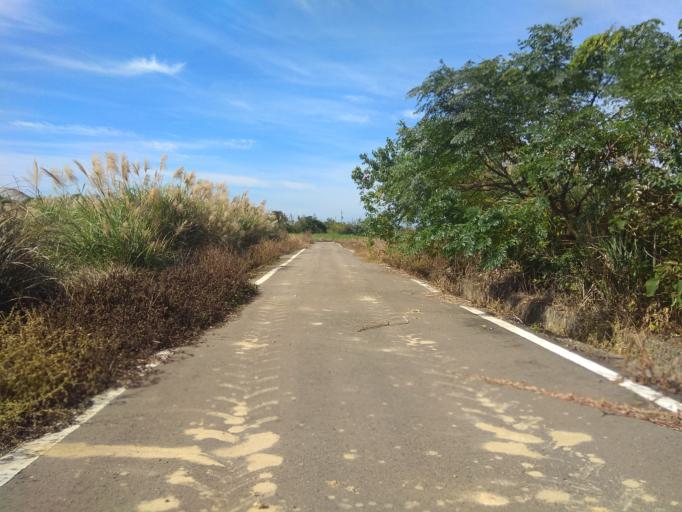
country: TW
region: Taiwan
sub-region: Hsinchu
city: Zhubei
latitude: 25.0198
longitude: 121.0676
